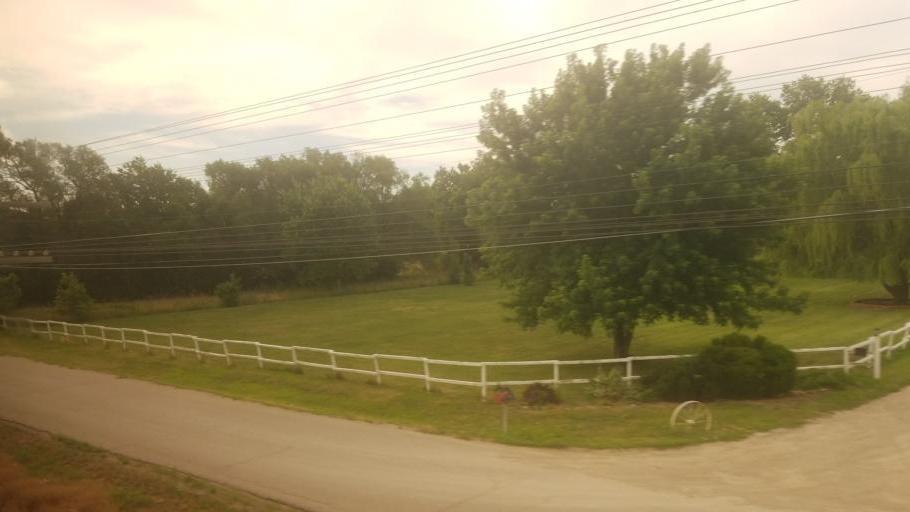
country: US
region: Kansas
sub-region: Shawnee County
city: Topeka
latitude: 39.0554
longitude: -95.6263
